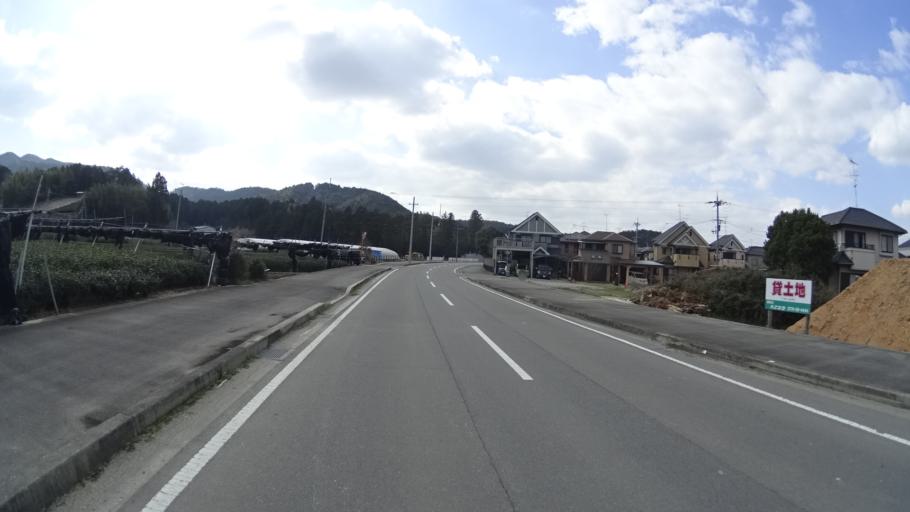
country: JP
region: Kyoto
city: Uji
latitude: 34.8381
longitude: 135.8579
